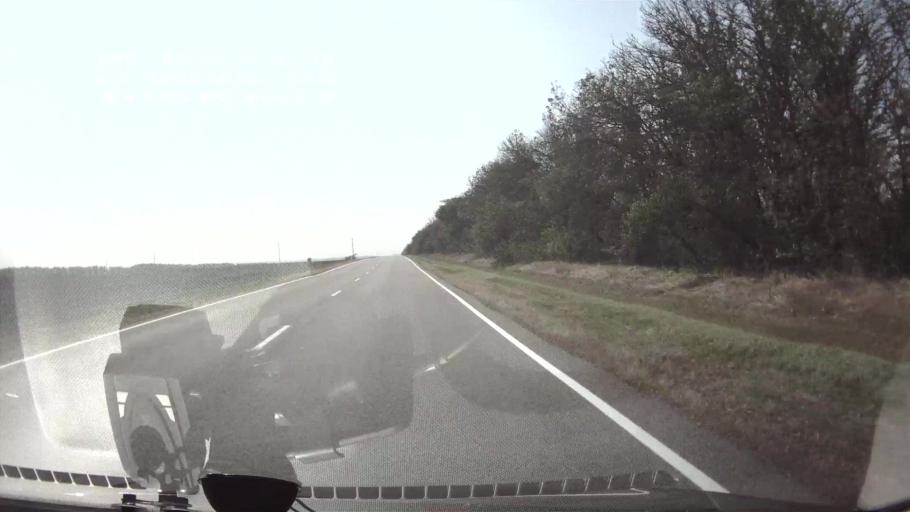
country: RU
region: Krasnodarskiy
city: Dmitriyevskaya
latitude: 45.7874
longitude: 40.7198
